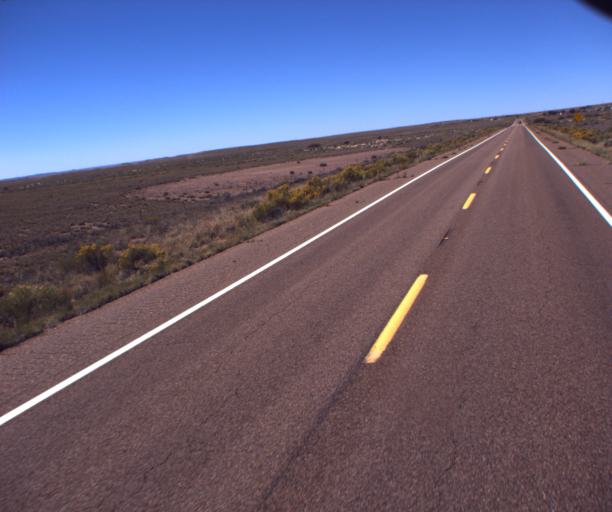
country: US
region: Arizona
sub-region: Navajo County
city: Holbrook
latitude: 34.7875
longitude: -109.8773
